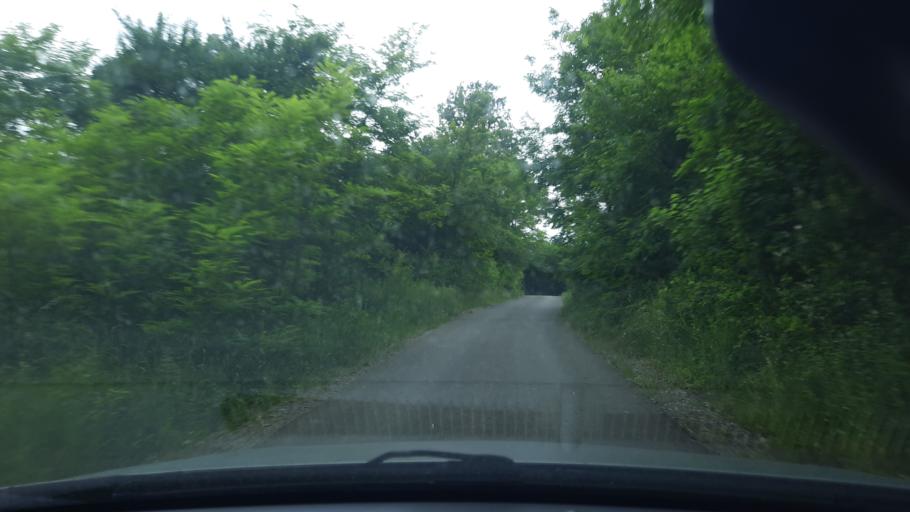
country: RS
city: Jarebice
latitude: 44.4946
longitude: 19.4778
